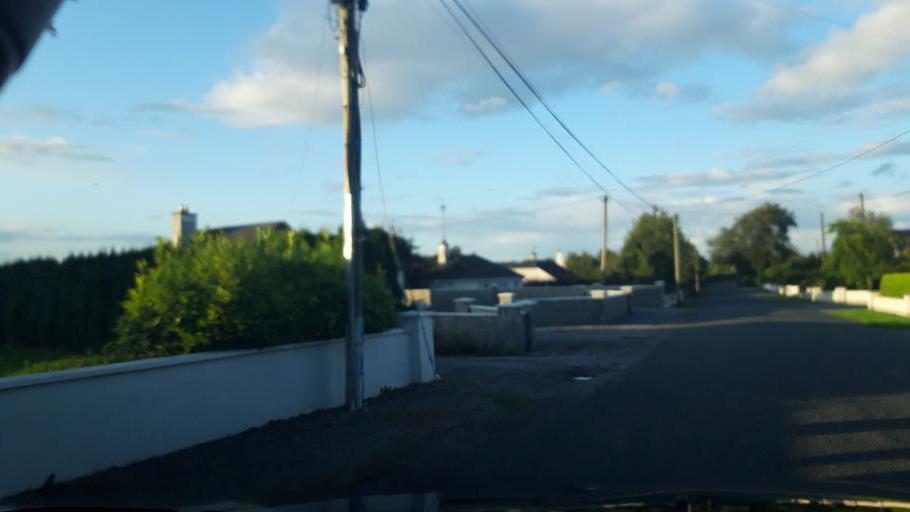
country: IE
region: Leinster
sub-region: An Iarmhi
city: Athlone
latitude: 53.4331
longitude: -7.8716
